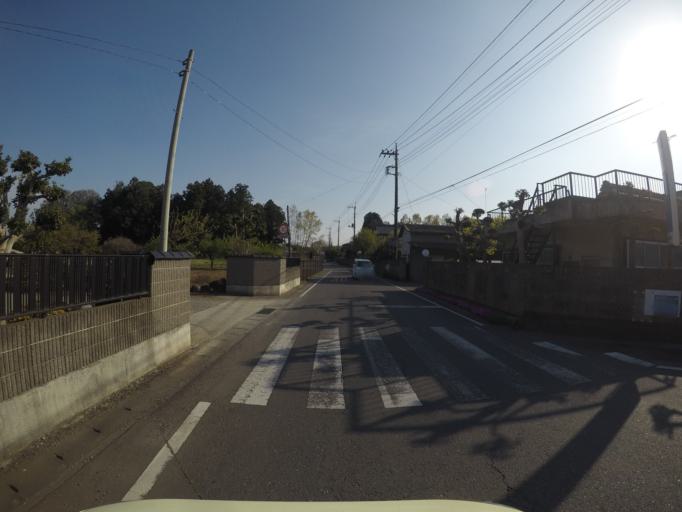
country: JP
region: Ibaraki
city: Ishige
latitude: 36.1716
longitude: 140.0174
